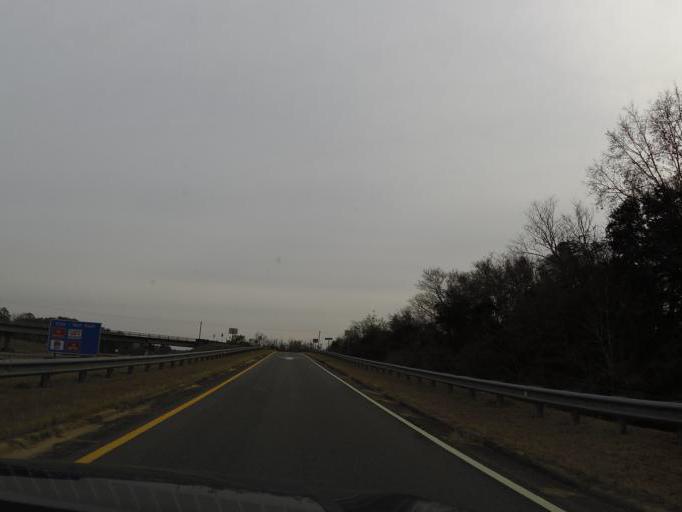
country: US
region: Georgia
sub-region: Decatur County
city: Bainbridge
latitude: 30.9122
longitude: -84.5954
